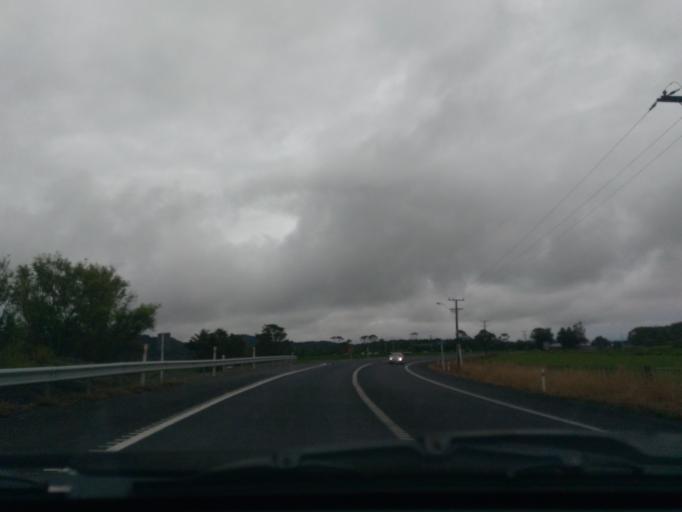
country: NZ
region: Northland
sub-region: Whangarei
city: Ruakaka
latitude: -36.0029
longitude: 174.4142
